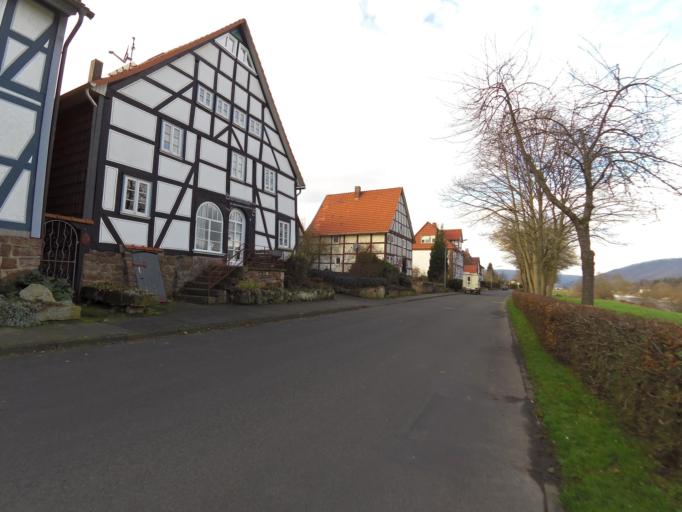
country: DE
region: Lower Saxony
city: Buhren
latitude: 51.4830
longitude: 9.6159
